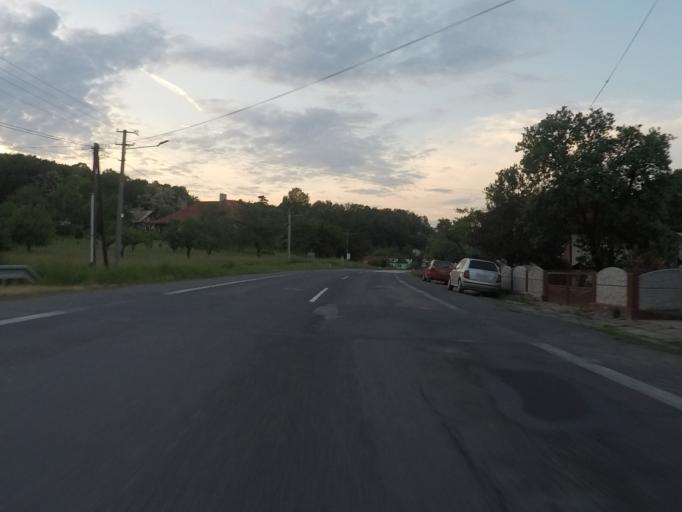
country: SK
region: Banskobystricky
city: Rimavska Sobota
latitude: 48.4710
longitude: 19.9499
